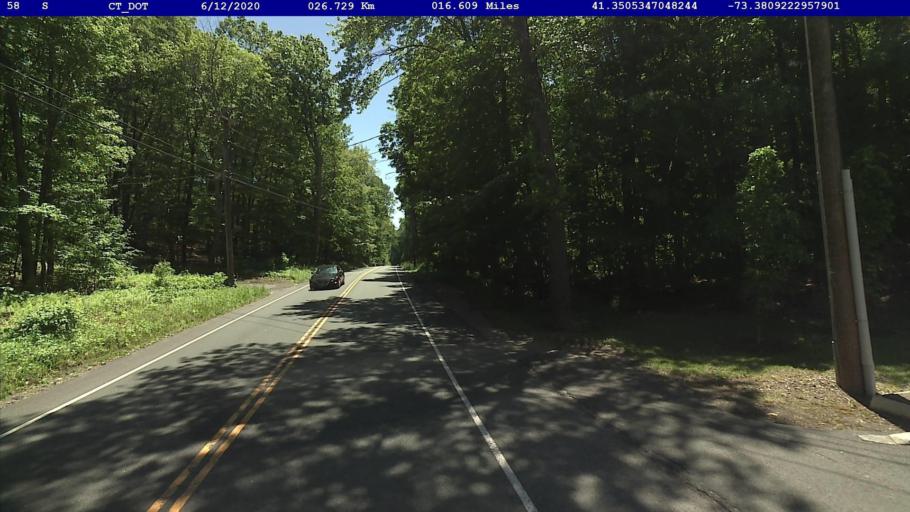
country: US
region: Connecticut
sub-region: Fairfield County
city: Bethel
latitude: 41.3505
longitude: -73.3809
